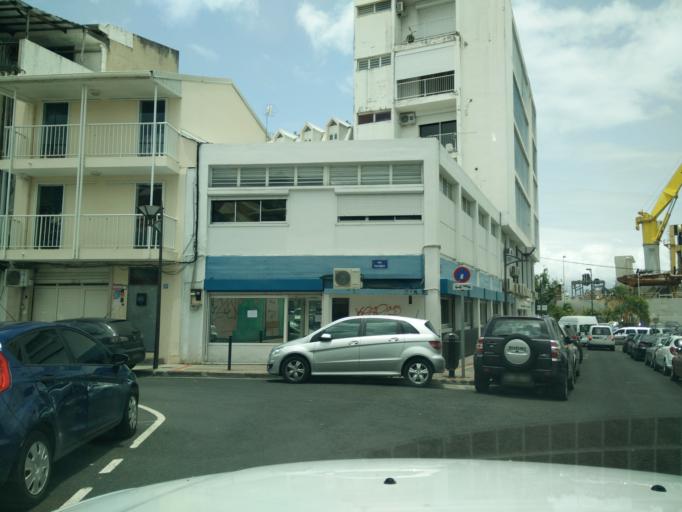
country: GP
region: Guadeloupe
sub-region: Guadeloupe
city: Pointe-a-Pitre
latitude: 16.2365
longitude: -61.5378
